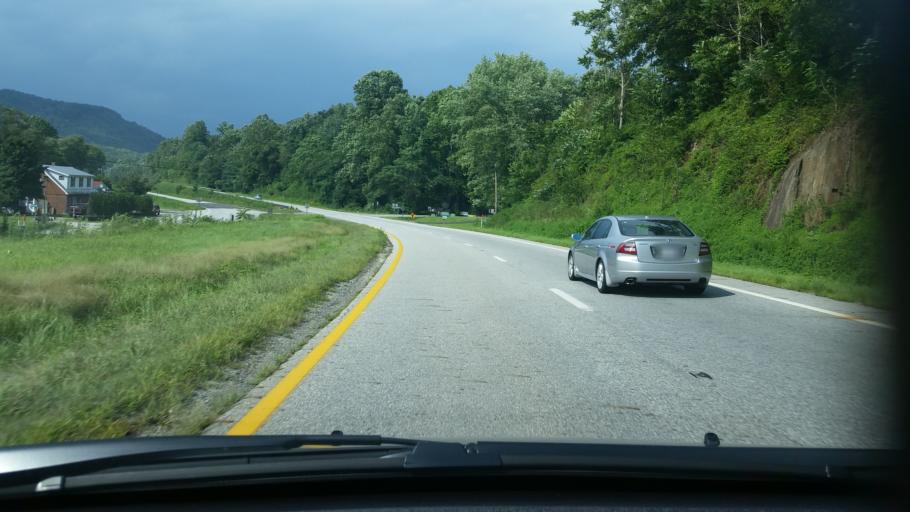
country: US
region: Virginia
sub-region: Nelson County
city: Lovingston
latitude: 37.7951
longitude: -78.8626
